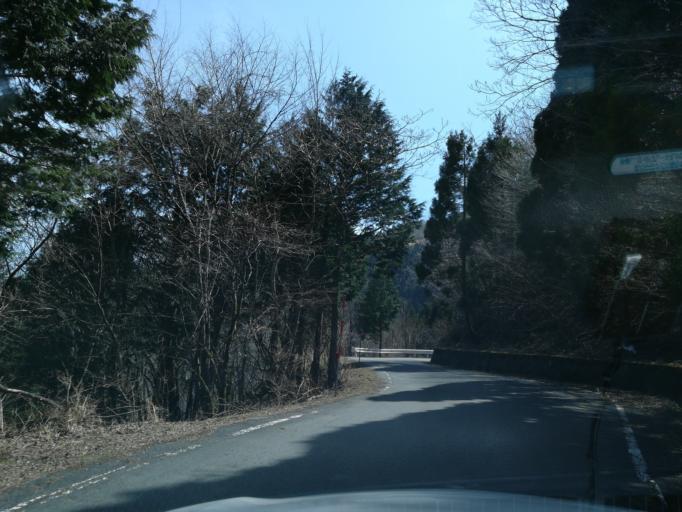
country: JP
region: Tokushima
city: Wakimachi
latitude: 33.8802
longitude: 134.0507
